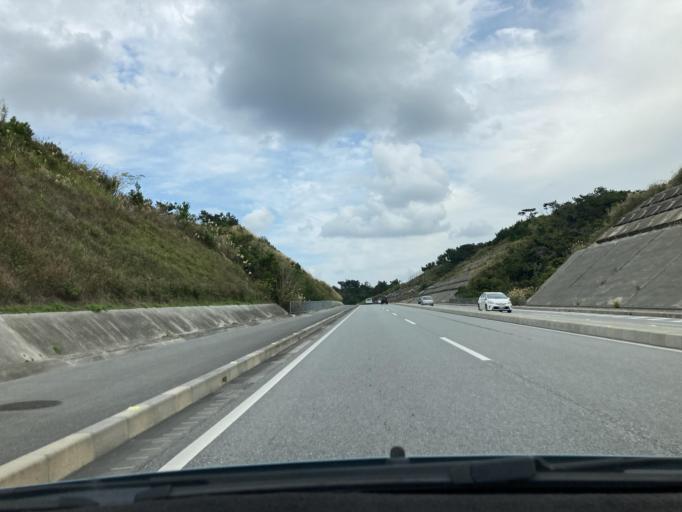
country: JP
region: Okinawa
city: Ishikawa
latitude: 26.4706
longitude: 127.8359
